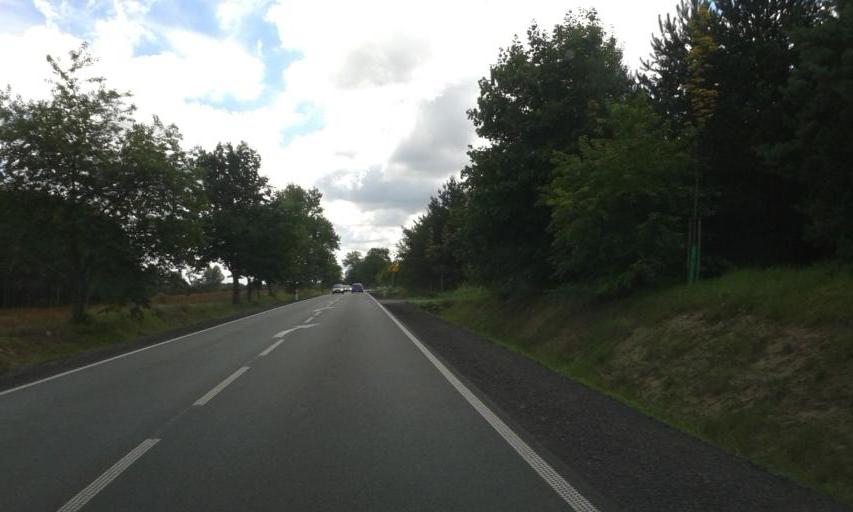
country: PL
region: West Pomeranian Voivodeship
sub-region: Powiat drawski
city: Czaplinek
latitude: 53.5319
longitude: 16.2922
